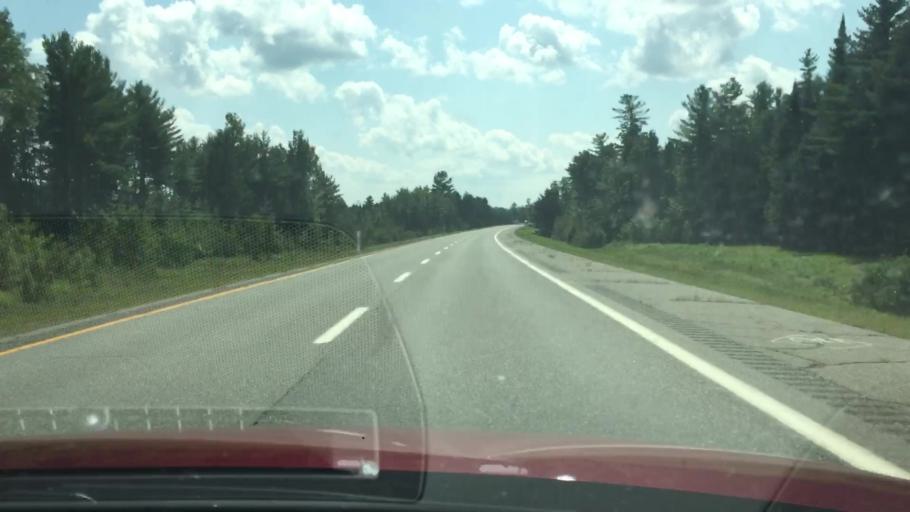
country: US
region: Maine
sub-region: Penobscot County
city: Medway
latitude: 45.5090
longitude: -68.5545
